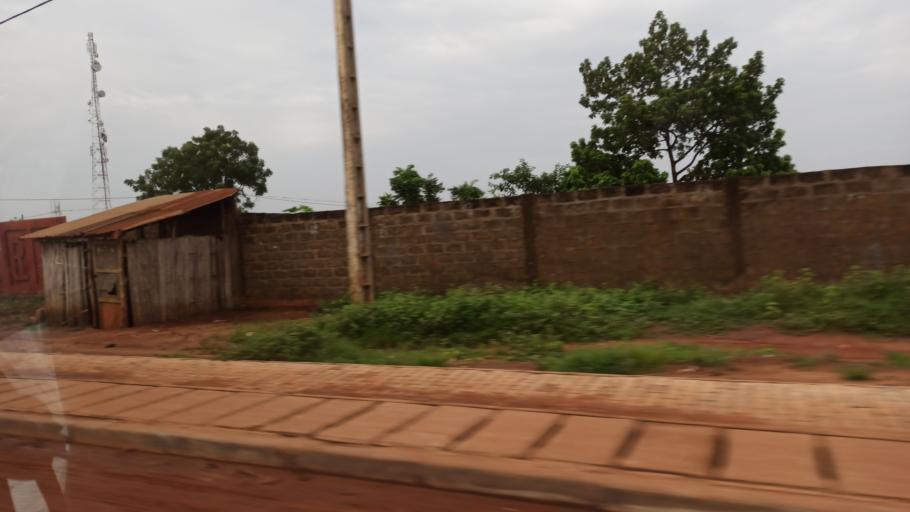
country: BJ
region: Queme
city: Porto-Novo
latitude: 6.5595
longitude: 2.5888
